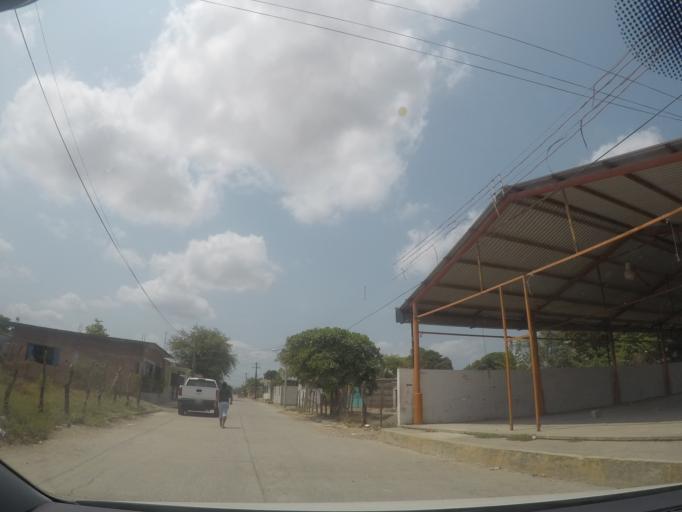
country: MX
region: Oaxaca
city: Asuncion Ixtaltepec
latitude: 16.4991
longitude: -95.0639
